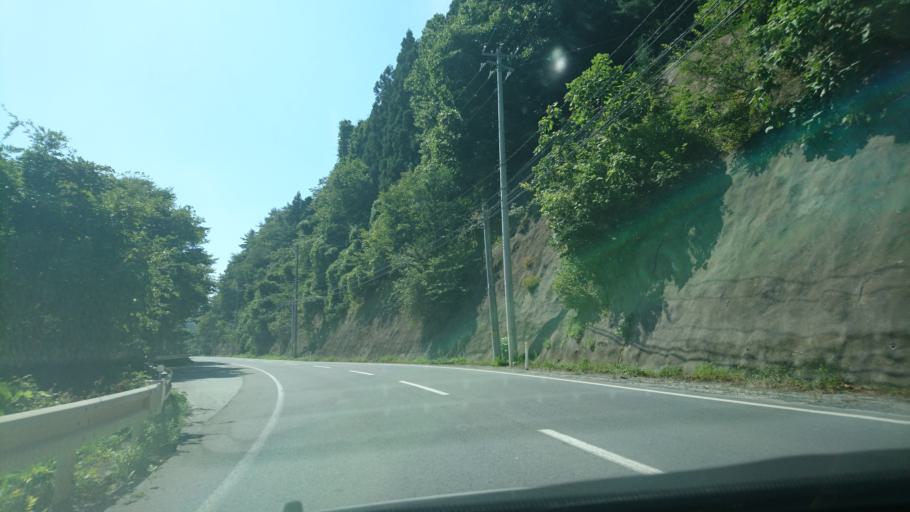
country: JP
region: Iwate
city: Ofunato
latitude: 39.0245
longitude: 141.5693
